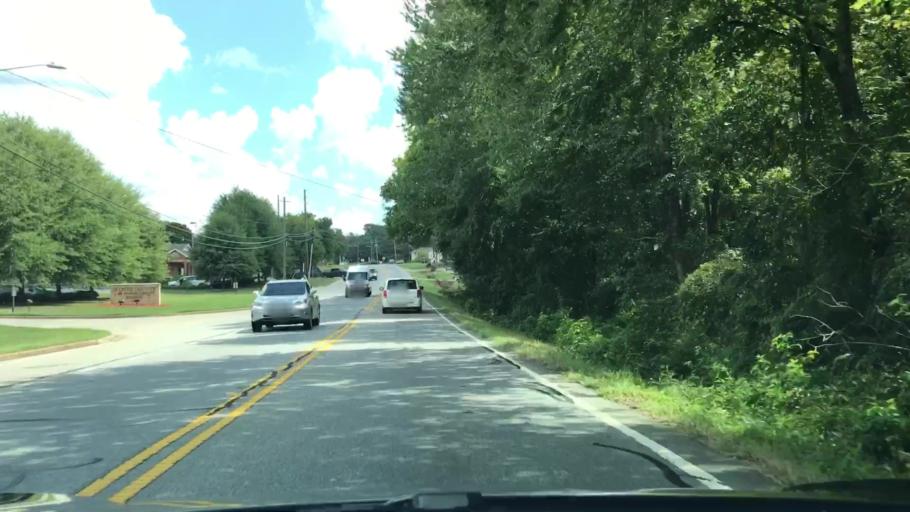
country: US
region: Georgia
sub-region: Oconee County
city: Watkinsville
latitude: 33.8676
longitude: -83.4161
